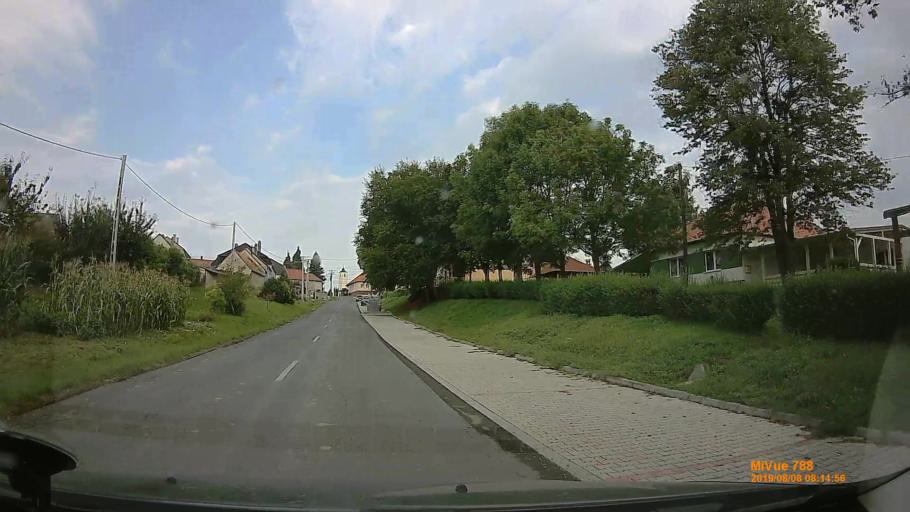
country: HU
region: Zala
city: Murakeresztur
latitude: 46.3972
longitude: 16.8498
